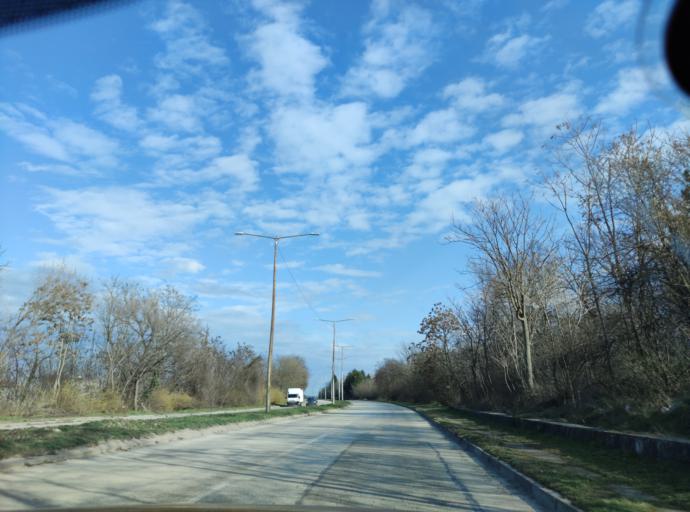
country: BG
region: Pleven
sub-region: Obshtina Dolna Mitropoliya
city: Dolna Mitropoliya
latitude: 43.4351
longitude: 24.5651
